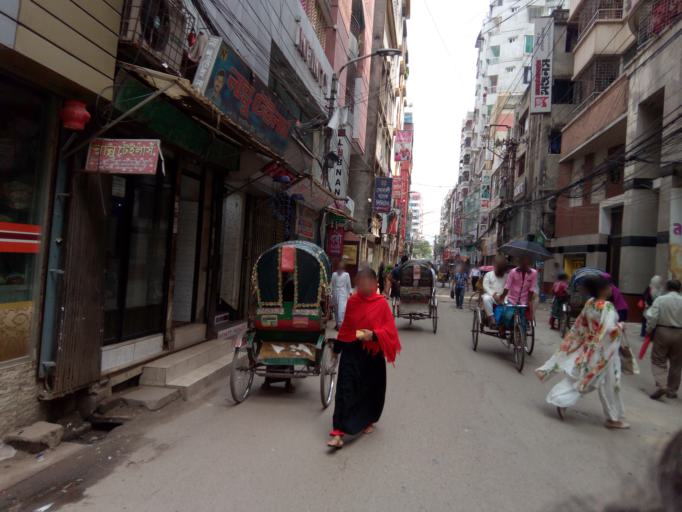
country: BD
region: Dhaka
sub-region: Dhaka
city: Dhaka
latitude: 23.7202
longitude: 90.4165
